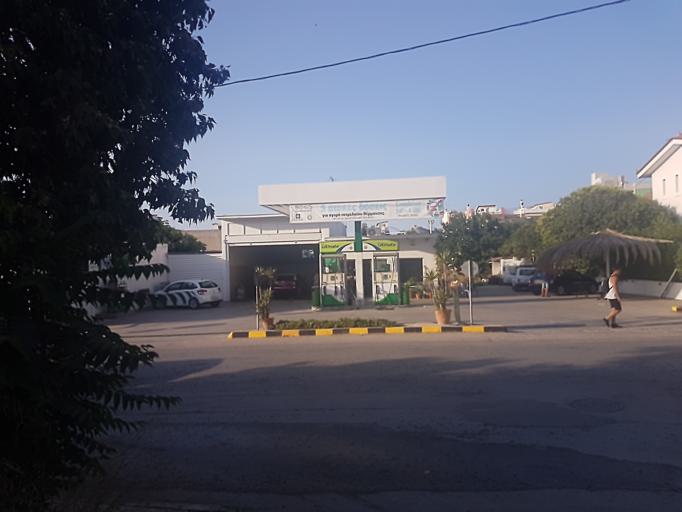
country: GR
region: Central Greece
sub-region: Nomos Evvoias
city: Vasilikon
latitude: 38.4246
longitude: 23.6737
